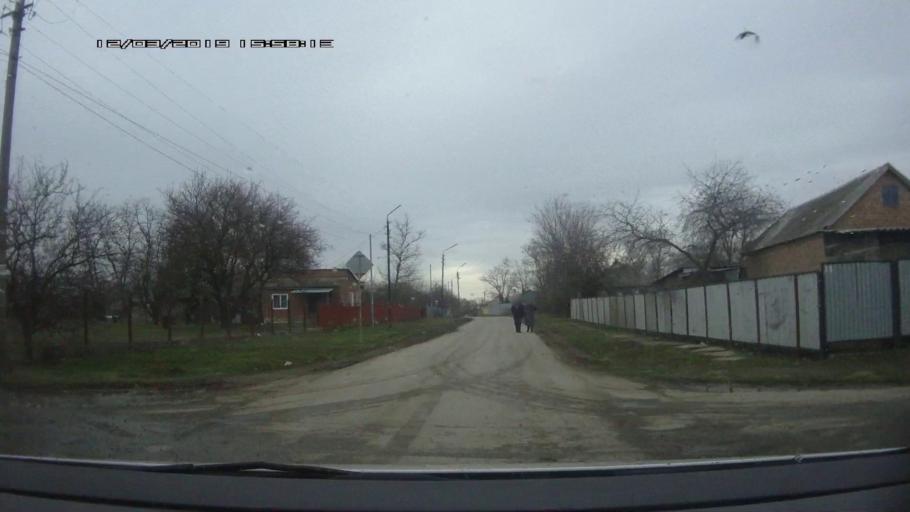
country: RU
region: Rostov
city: Novobataysk
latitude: 46.9024
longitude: 39.7894
